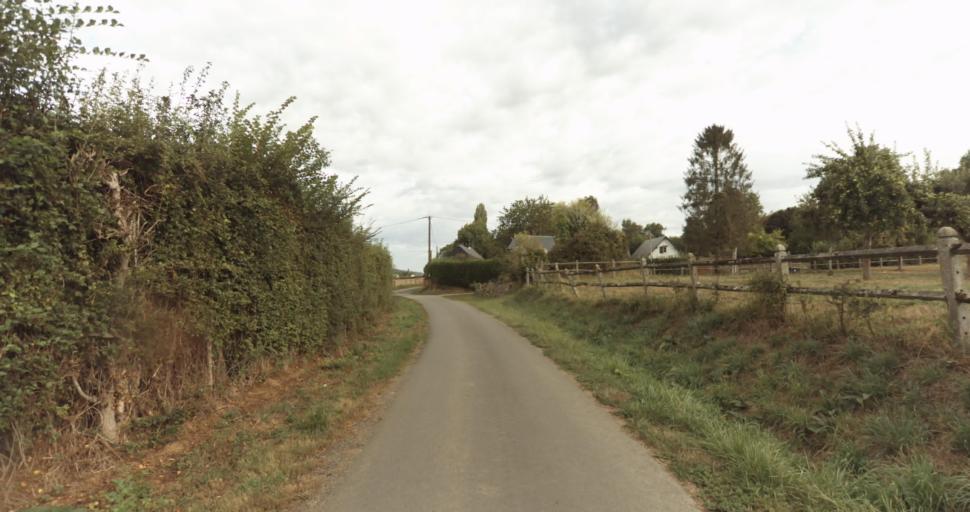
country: FR
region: Lower Normandy
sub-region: Departement de l'Orne
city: Vimoutiers
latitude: 48.9474
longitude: 0.2731
